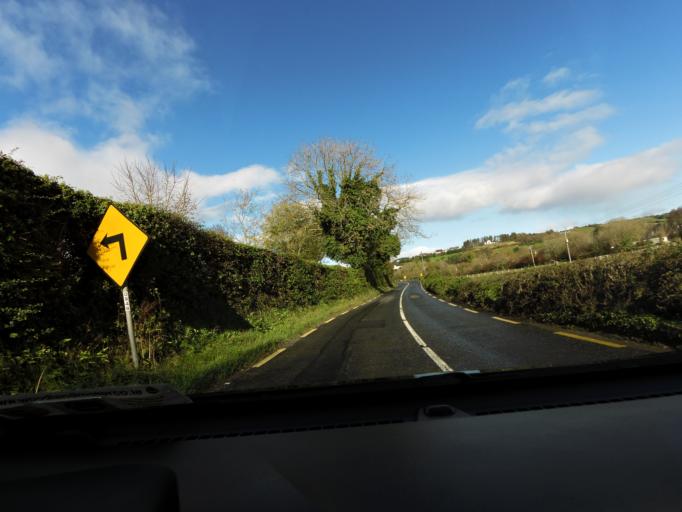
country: IE
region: Connaught
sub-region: Maigh Eo
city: Westport
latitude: 53.8085
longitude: -9.5285
